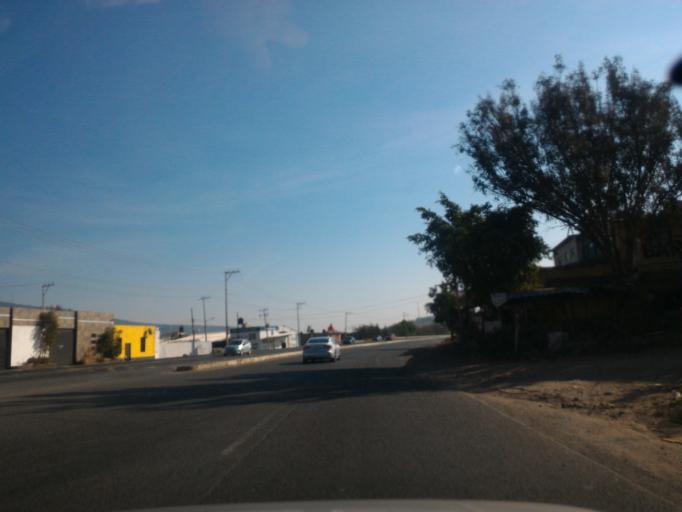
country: MX
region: Jalisco
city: Atotonilquillo
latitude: 20.3921
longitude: -103.1316
